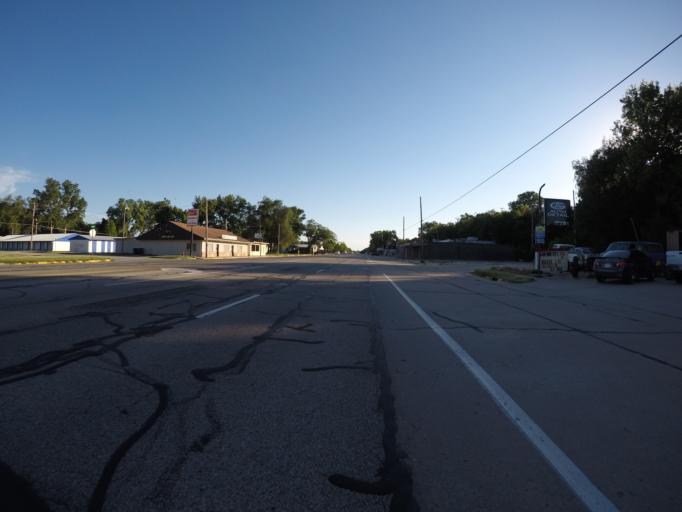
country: US
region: Kansas
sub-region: Riley County
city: Ogden
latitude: 39.1142
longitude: -96.7139
